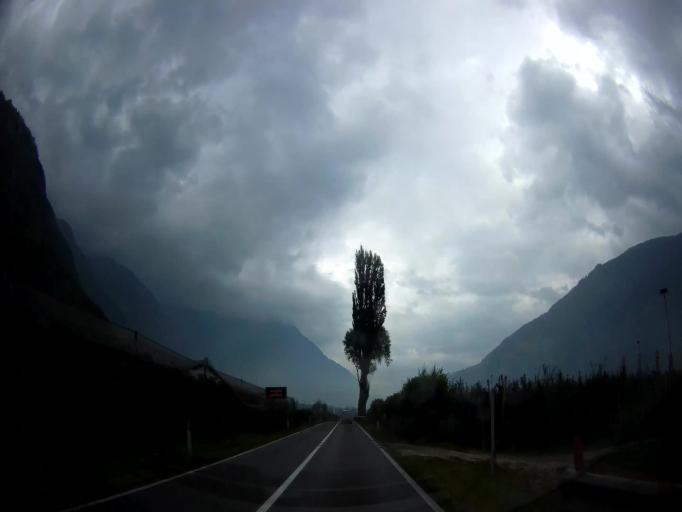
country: IT
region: Trentino-Alto Adige
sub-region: Bolzano
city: Plaus
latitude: 46.6640
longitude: 11.0459
